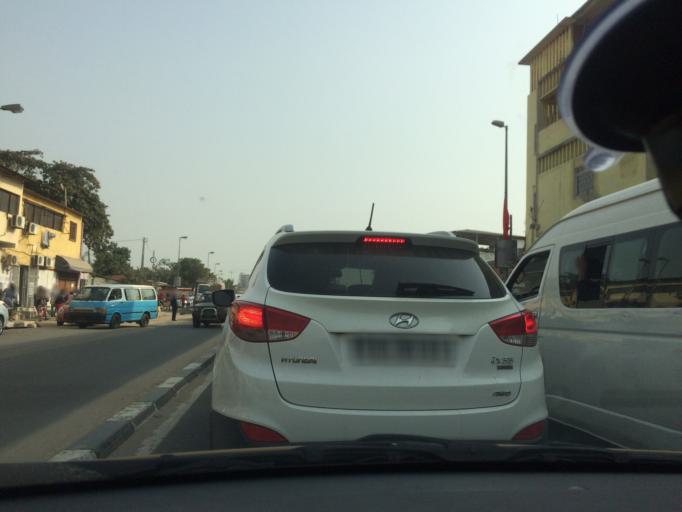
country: AO
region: Luanda
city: Luanda
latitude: -8.8287
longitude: 13.2219
